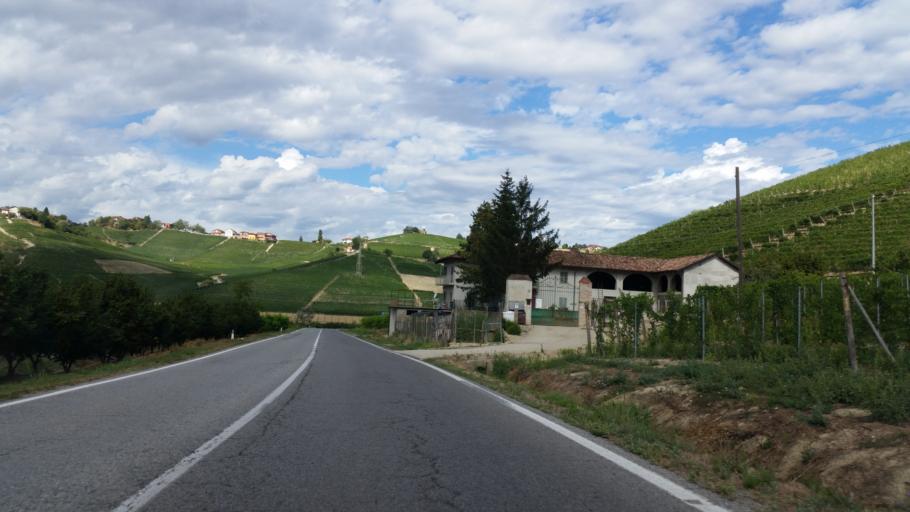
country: IT
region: Piedmont
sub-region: Provincia di Cuneo
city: Barbaresco
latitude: 44.7279
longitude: 8.0993
